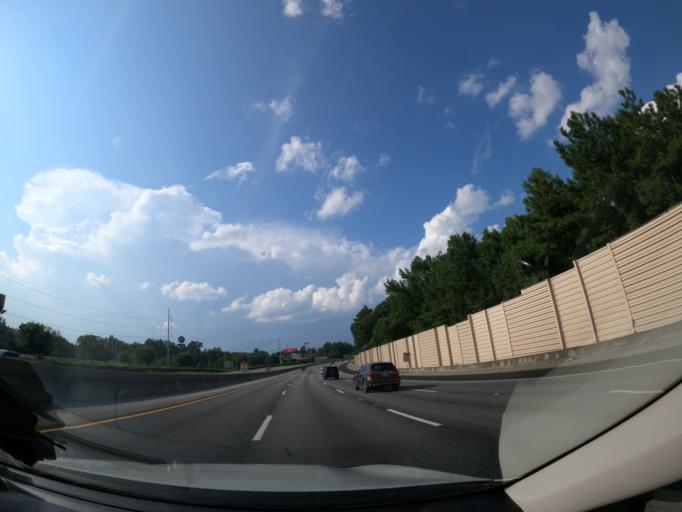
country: US
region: Georgia
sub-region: Columbia County
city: Martinez
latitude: 33.4739
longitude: -82.0860
